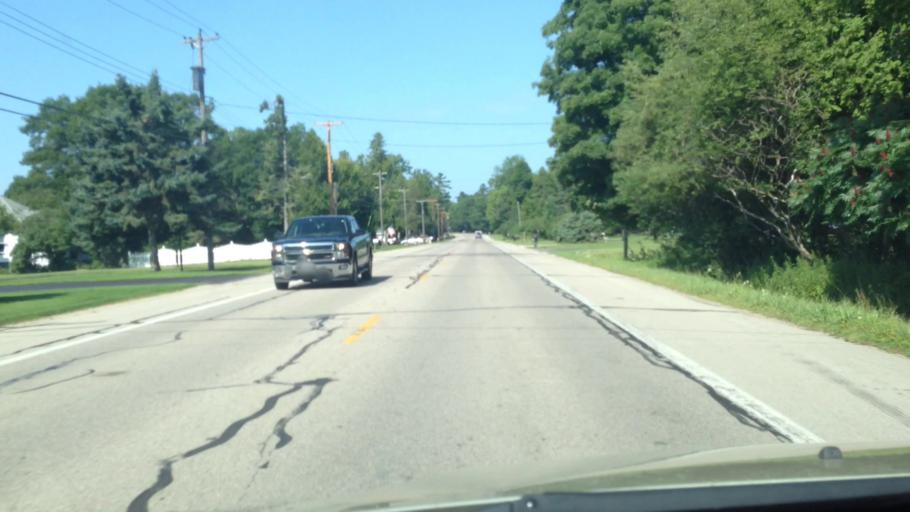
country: US
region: Michigan
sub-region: Delta County
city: Escanaba
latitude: 45.6867
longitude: -87.1098
